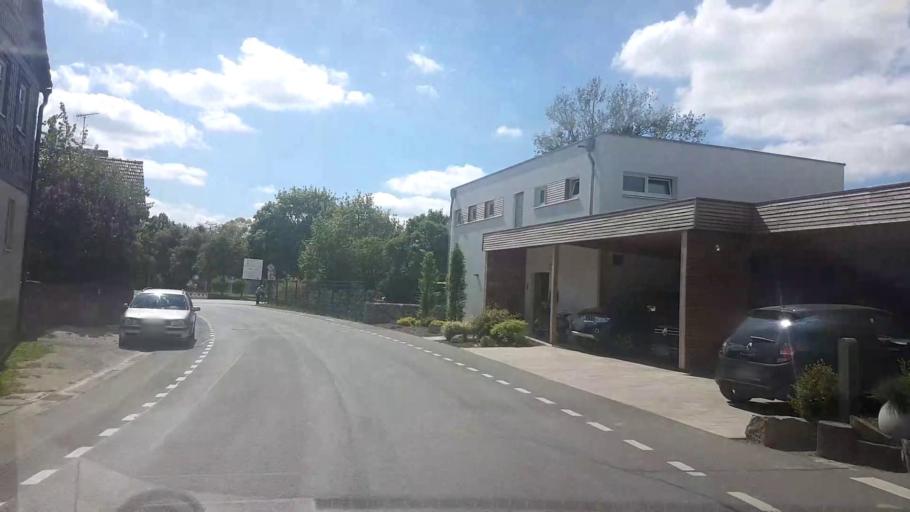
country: DE
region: Bavaria
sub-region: Upper Franconia
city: Grossheirath
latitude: 50.1635
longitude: 10.9358
